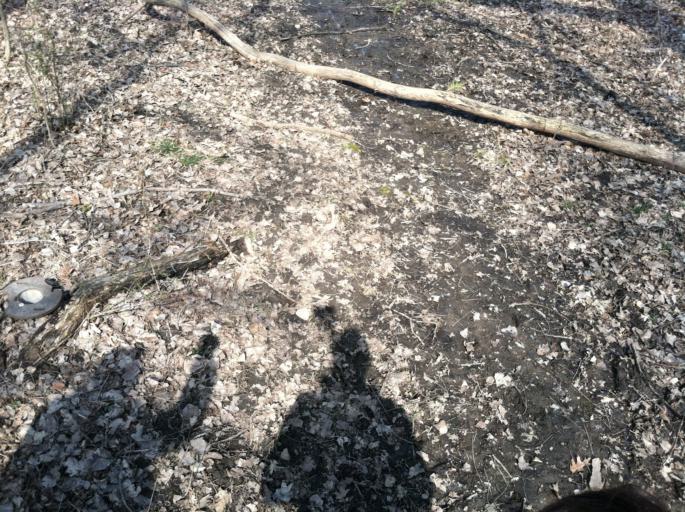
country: US
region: Illinois
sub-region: Cook County
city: River Forest
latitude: 41.8999
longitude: -87.8302
